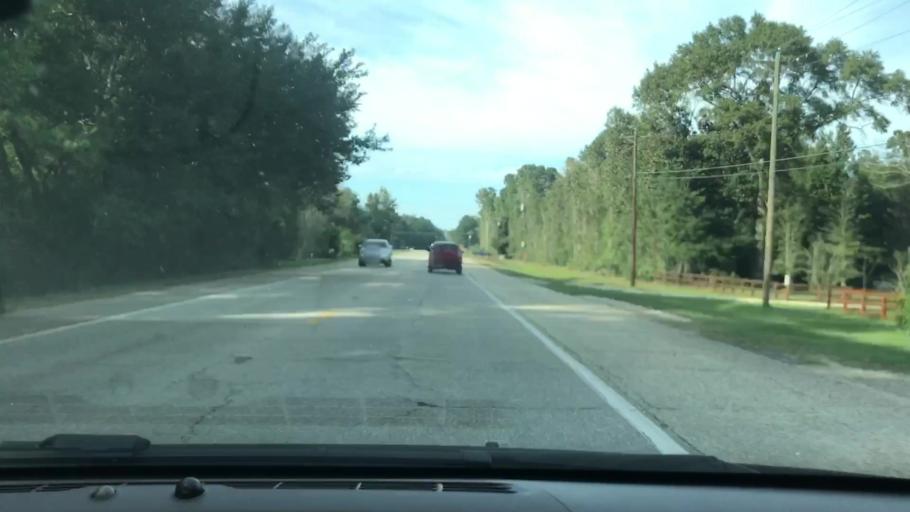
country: US
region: Mississippi
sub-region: Pearl River County
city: Nicholson
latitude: 30.4914
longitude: -89.8111
